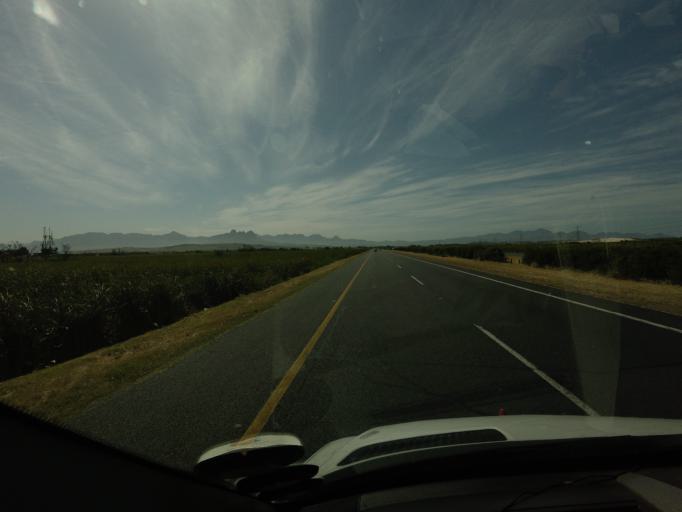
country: ZA
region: Western Cape
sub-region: Cape Winelands District Municipality
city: Stellenbosch
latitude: -34.0353
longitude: 18.7137
